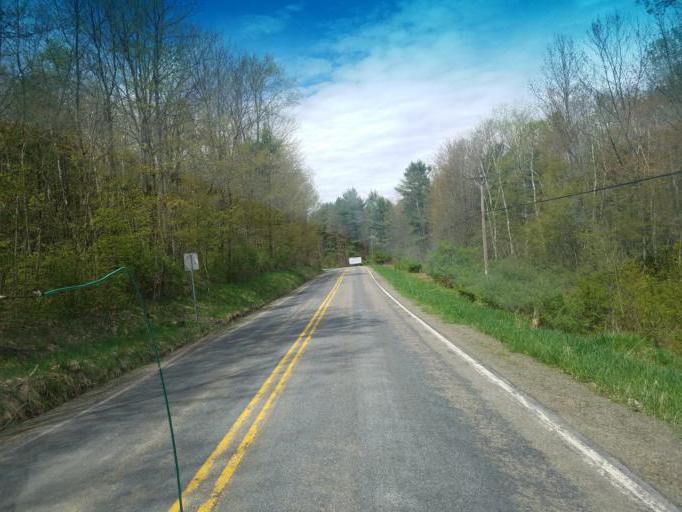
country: US
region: Pennsylvania
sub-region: Tioga County
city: Wellsboro
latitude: 41.6973
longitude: -77.4179
